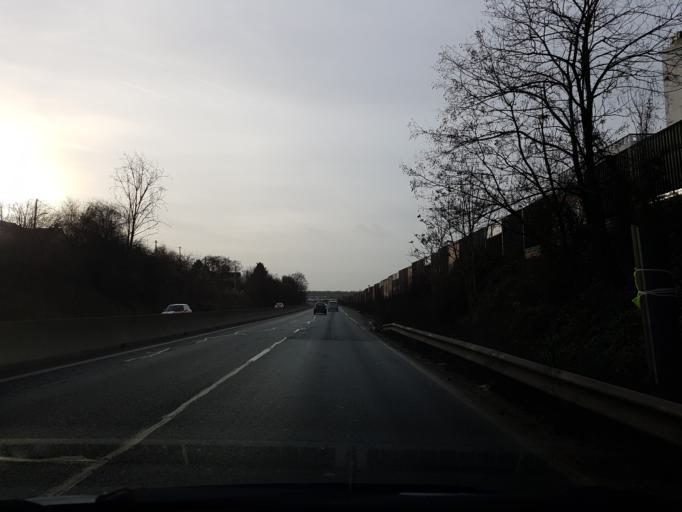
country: FR
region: Ile-de-France
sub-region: Departement de l'Essonne
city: Montgeron
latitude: 48.7038
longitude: 2.4437
